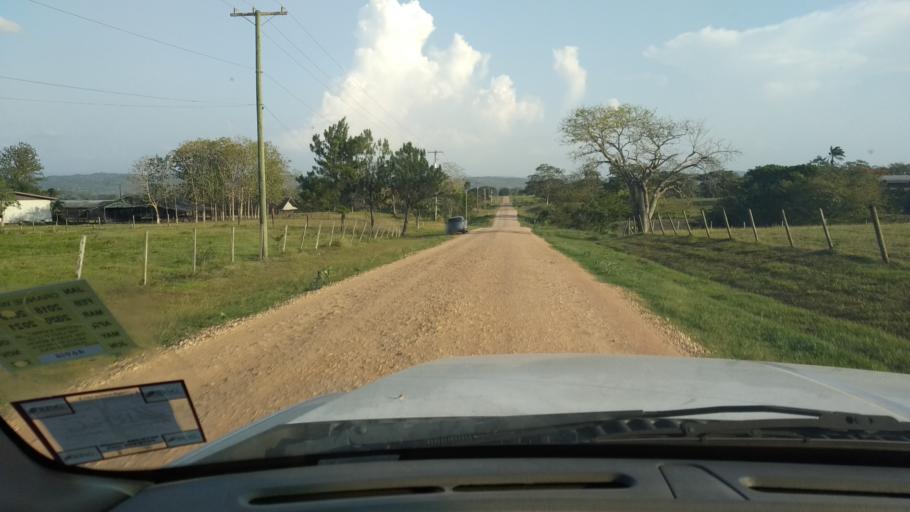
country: BZ
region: Cayo
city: San Ignacio
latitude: 17.2359
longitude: -88.9875
